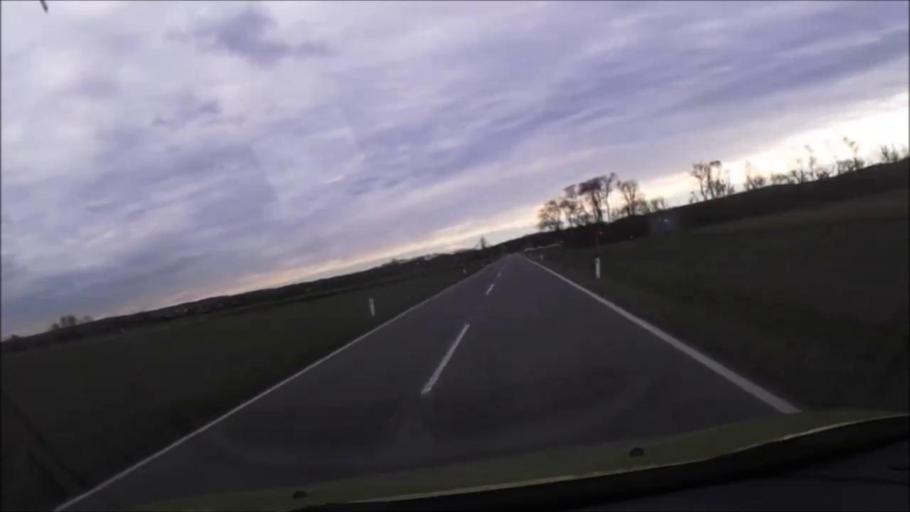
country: AT
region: Burgenland
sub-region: Eisenstadt-Umgebung
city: Leithaprodersdorf
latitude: 47.9468
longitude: 16.4585
